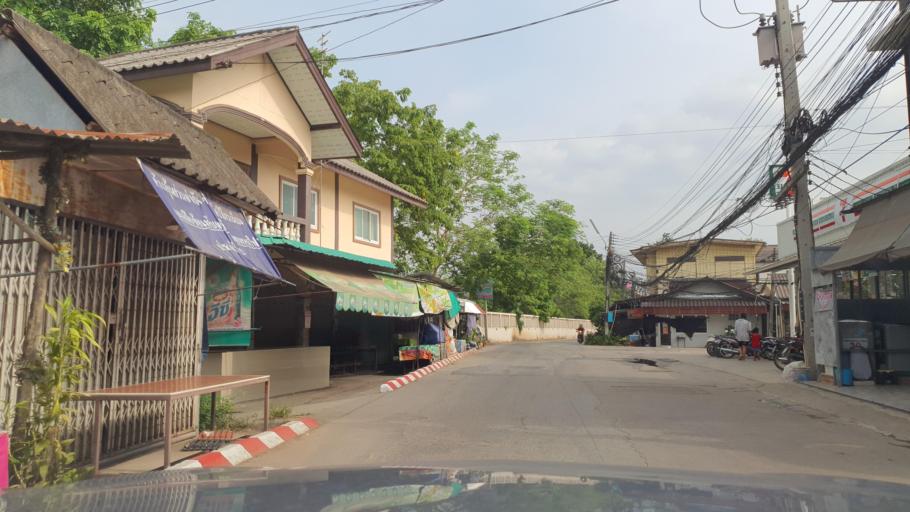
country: TH
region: Phitsanulok
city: Phitsanulok
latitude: 16.8485
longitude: 100.2564
